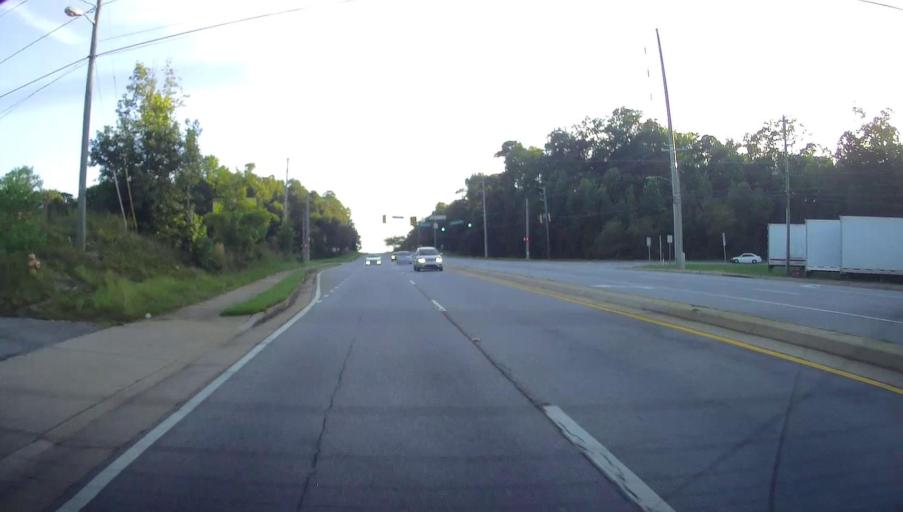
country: US
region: Georgia
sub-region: Muscogee County
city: Columbus
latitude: 32.5142
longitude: -84.8879
